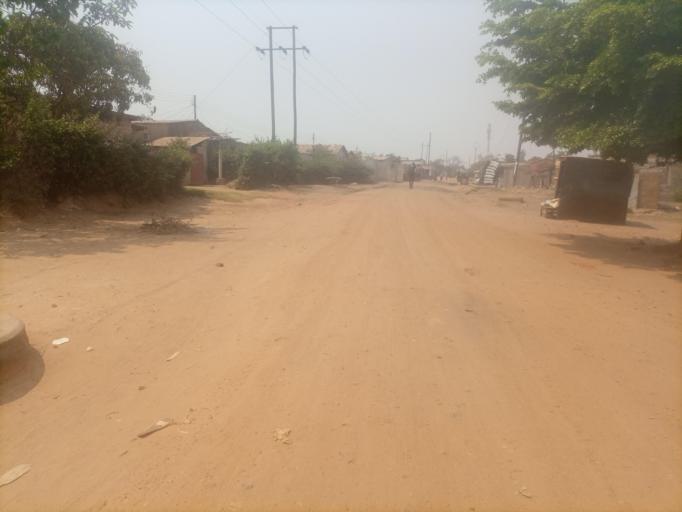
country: ZM
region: Lusaka
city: Lusaka
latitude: -15.3961
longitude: 28.3682
